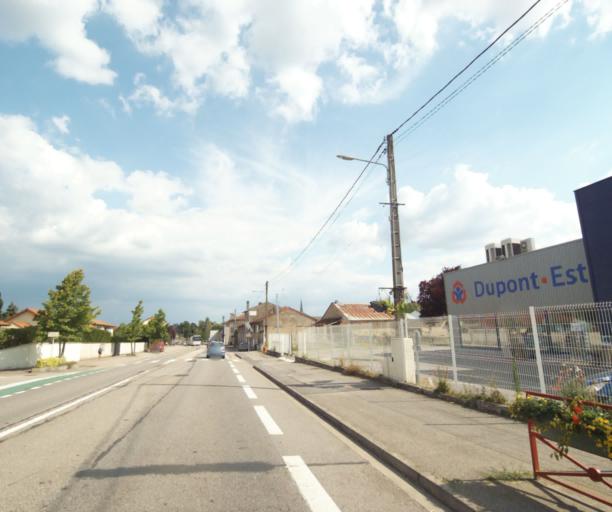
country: FR
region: Lorraine
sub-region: Departement de Meurthe-et-Moselle
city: Chanteheux
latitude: 48.5745
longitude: 6.5275
